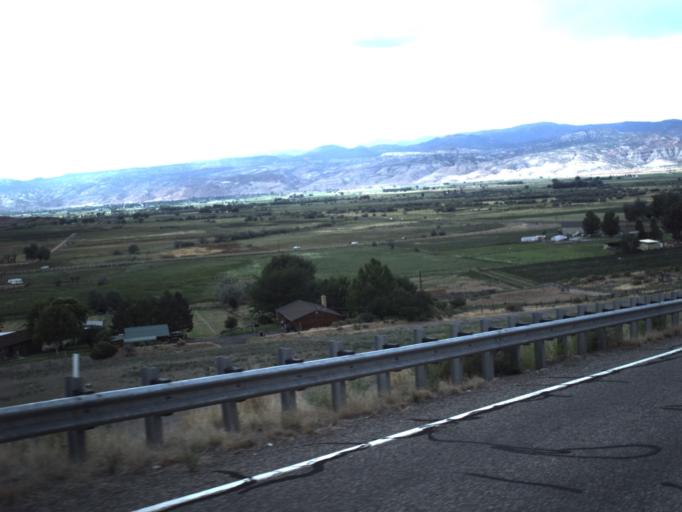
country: US
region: Utah
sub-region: Sevier County
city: Richfield
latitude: 38.7711
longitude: -111.9825
